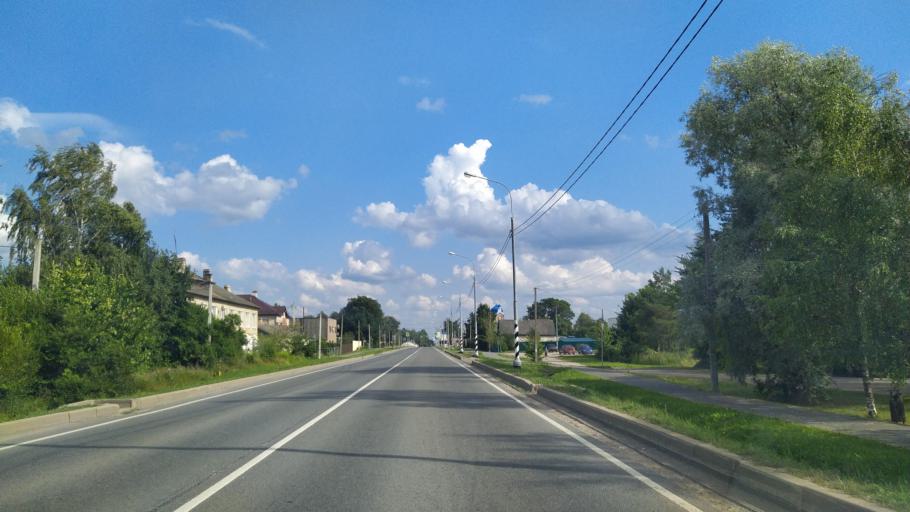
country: RU
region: Novgorod
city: Shimsk
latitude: 58.2126
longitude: 30.7120
